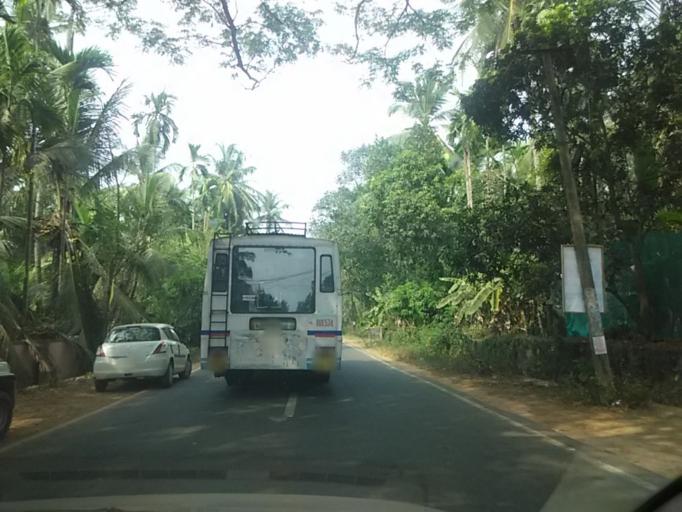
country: IN
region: Kerala
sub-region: Kozhikode
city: Naduvannur
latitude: 11.4598
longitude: 75.7721
